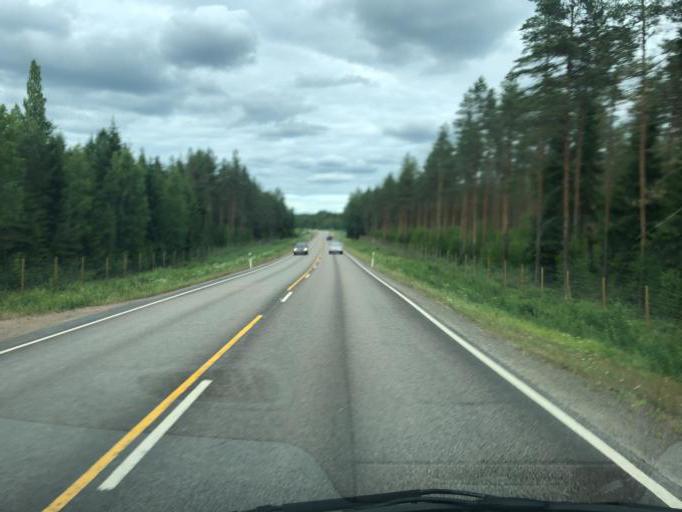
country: FI
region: Kymenlaakso
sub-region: Kouvola
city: Kouvola
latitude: 61.0236
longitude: 26.9744
